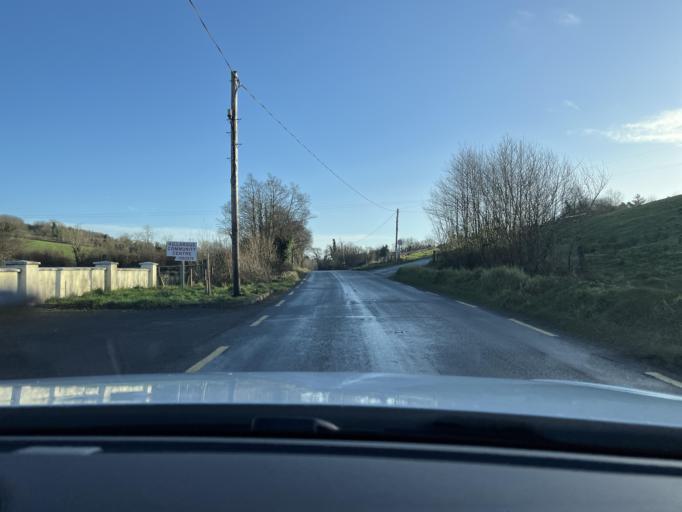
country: IE
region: Connaught
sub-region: County Leitrim
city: Manorhamilton
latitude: 54.2402
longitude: -8.2203
